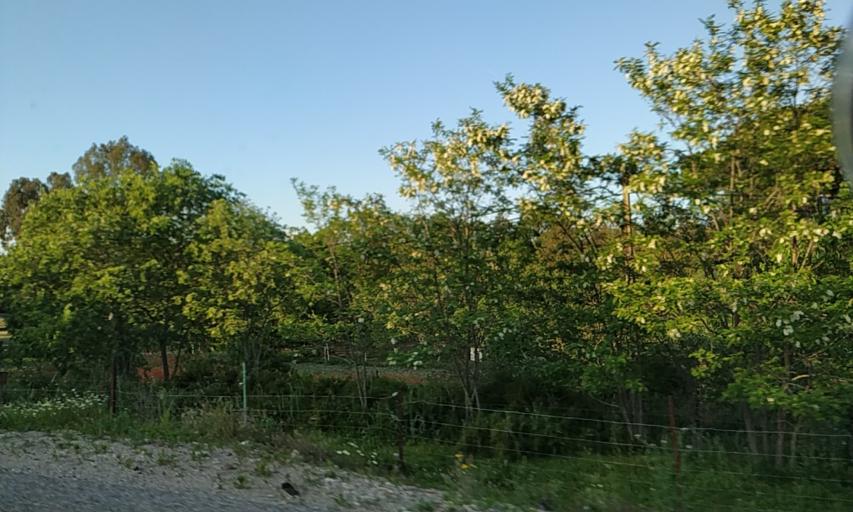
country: ES
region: Extremadura
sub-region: Provincia de Caceres
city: Valencia de Alcantara
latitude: 39.3951
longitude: -7.2471
